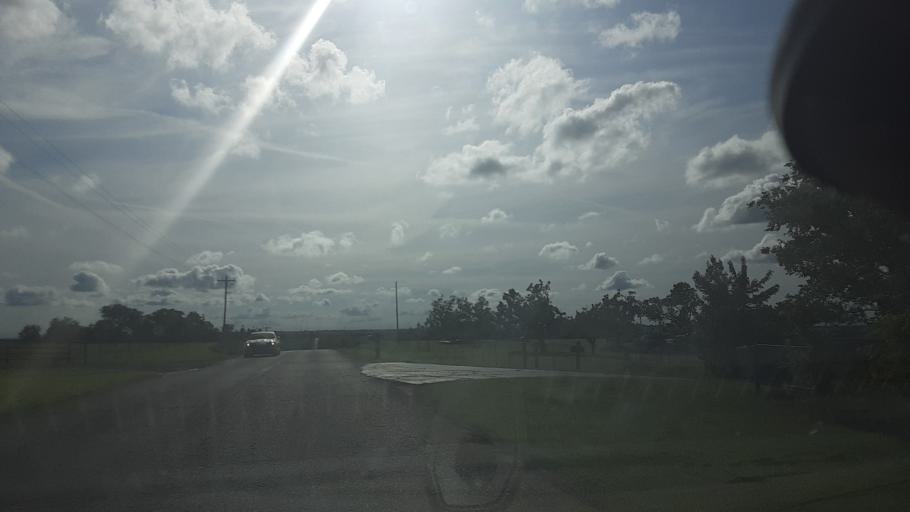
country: US
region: Oklahoma
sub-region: Logan County
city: Langston
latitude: 36.0578
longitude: -97.3807
